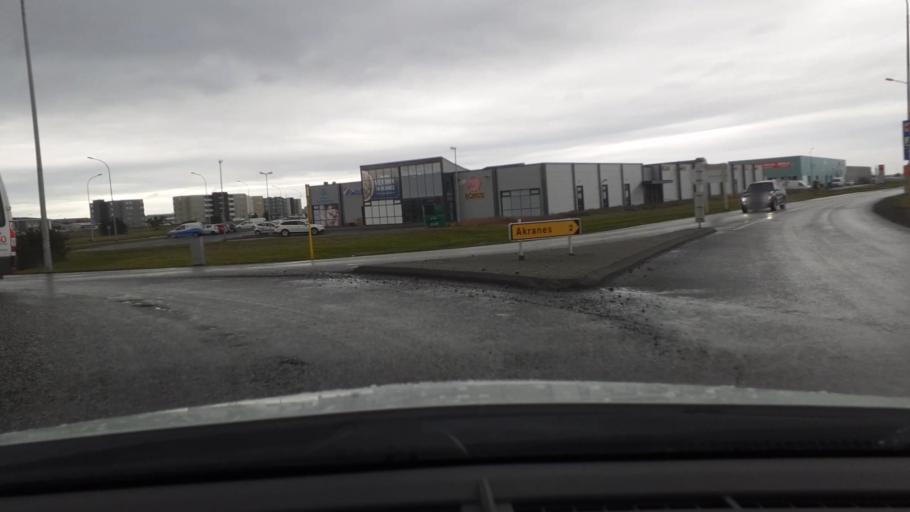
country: IS
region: West
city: Akranes
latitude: 64.3278
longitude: -22.0530
